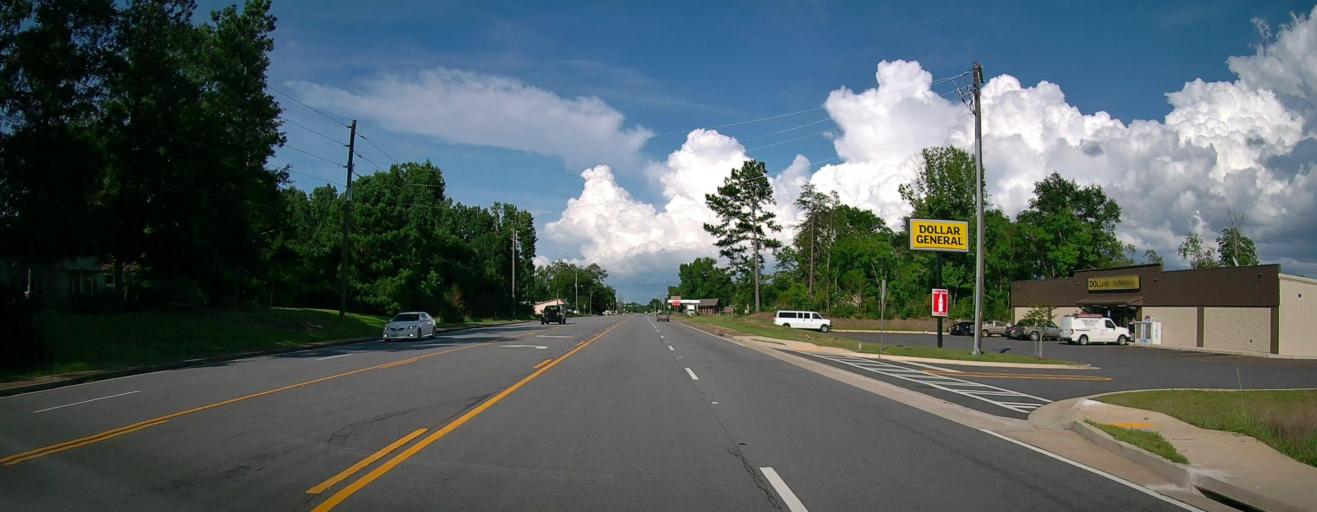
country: US
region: Georgia
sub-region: Talbot County
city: Talbotton
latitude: 32.5763
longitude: -84.5579
